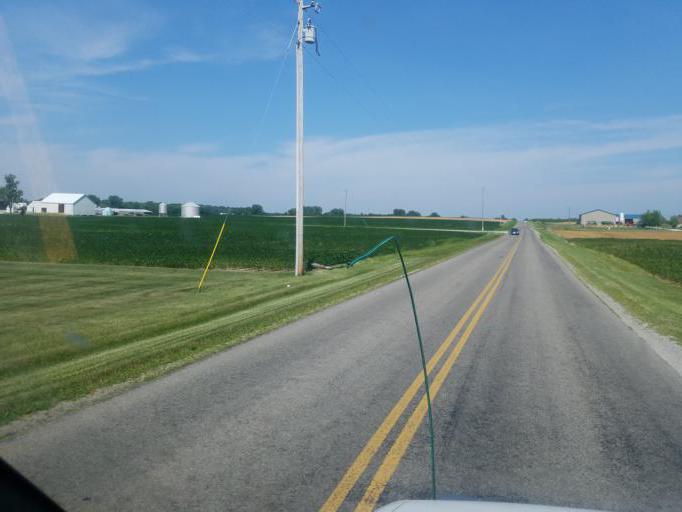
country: US
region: Ohio
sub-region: Shelby County
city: Botkins
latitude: 40.4971
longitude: -84.1482
